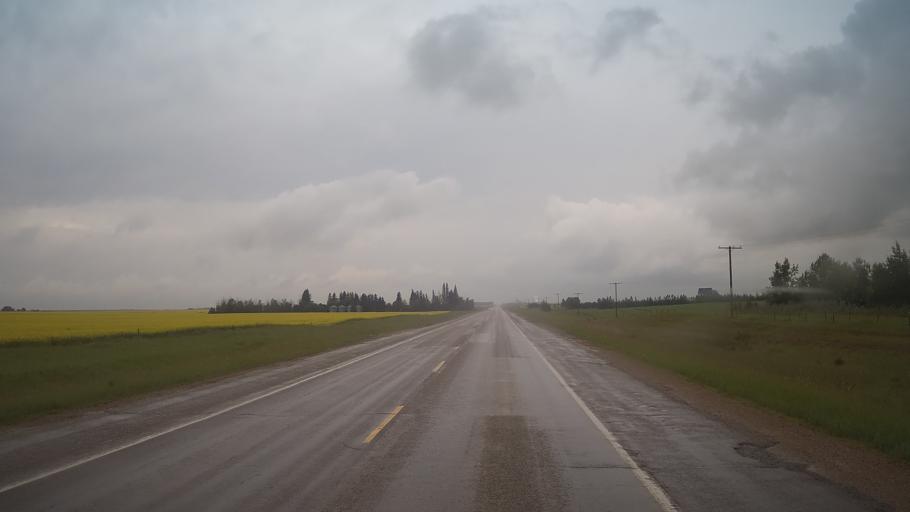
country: CA
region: Saskatchewan
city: Unity
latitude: 52.4350
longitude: -109.0306
